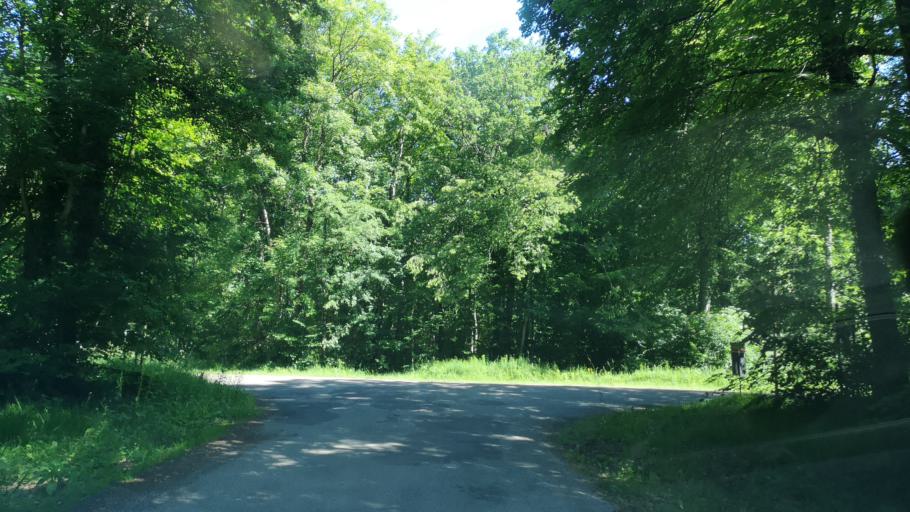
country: FR
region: Lorraine
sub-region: Departement de la Meuse
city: Vigneulles-les-Hattonchatel
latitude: 49.0274
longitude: 5.6464
